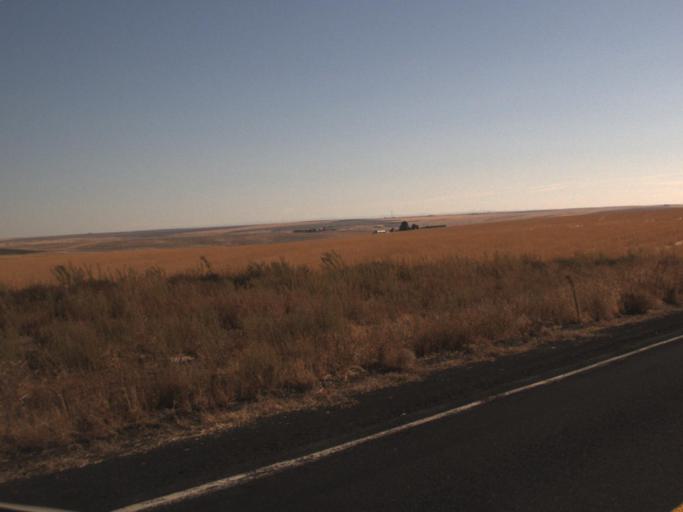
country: US
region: Washington
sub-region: Adams County
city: Ritzville
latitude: 47.0223
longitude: -118.6635
